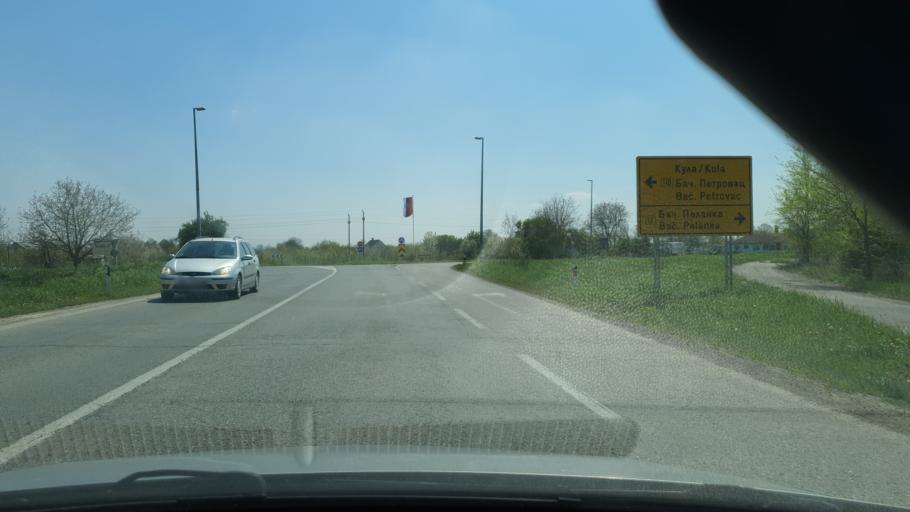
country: RS
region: Autonomna Pokrajina Vojvodina
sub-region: Zapadnobacki Okrug
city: Odzaci
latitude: 45.5000
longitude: 19.2667
